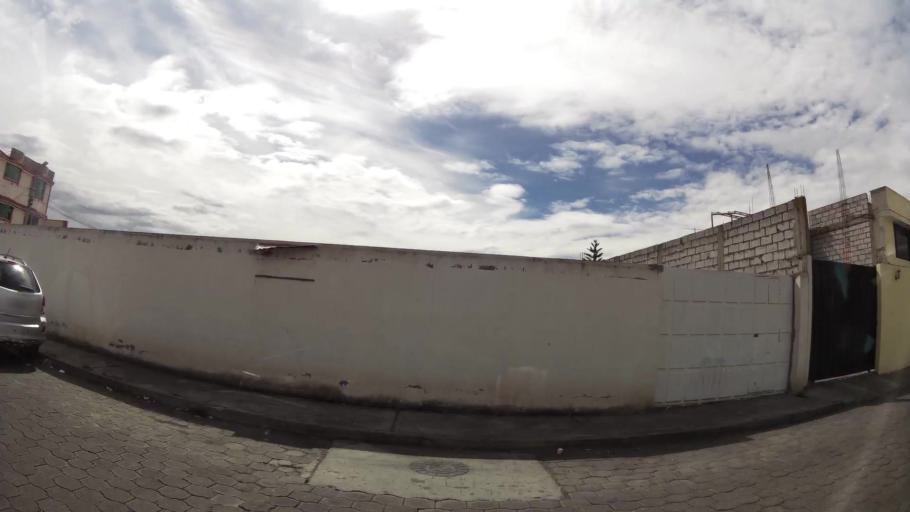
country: EC
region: Cotopaxi
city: Latacunga
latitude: -0.9319
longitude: -78.6020
